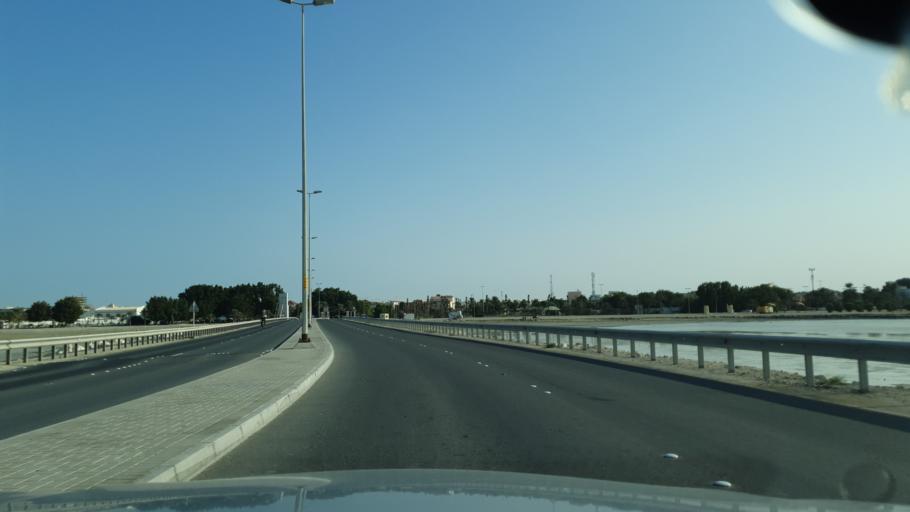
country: BH
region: Manama
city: Jidd Hafs
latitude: 26.2264
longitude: 50.4574
